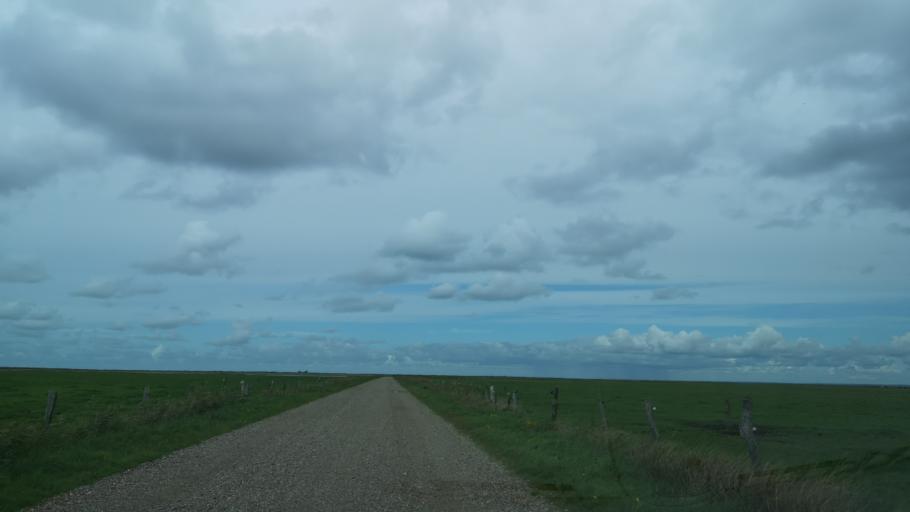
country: DK
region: Central Jutland
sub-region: Ringkobing-Skjern Kommune
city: Hvide Sande
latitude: 55.8639
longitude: 8.2203
